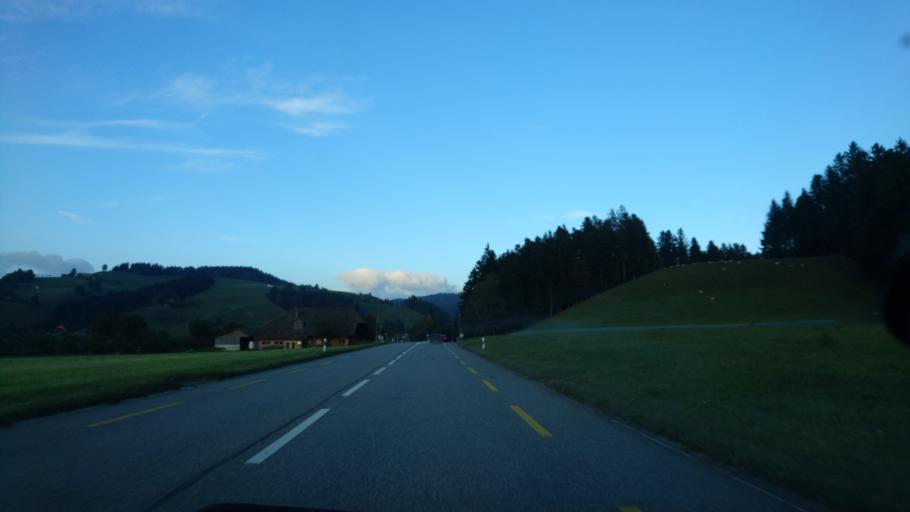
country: CH
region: Bern
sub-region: Emmental District
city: Lauperswil
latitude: 46.9397
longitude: 7.7550
